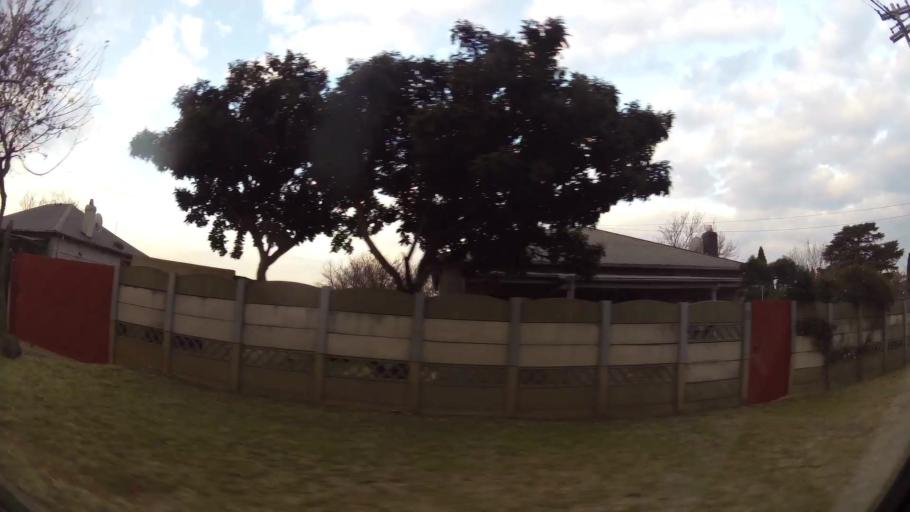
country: ZA
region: Gauteng
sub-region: Ekurhuleni Metropolitan Municipality
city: Germiston
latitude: -26.1888
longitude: 28.1666
